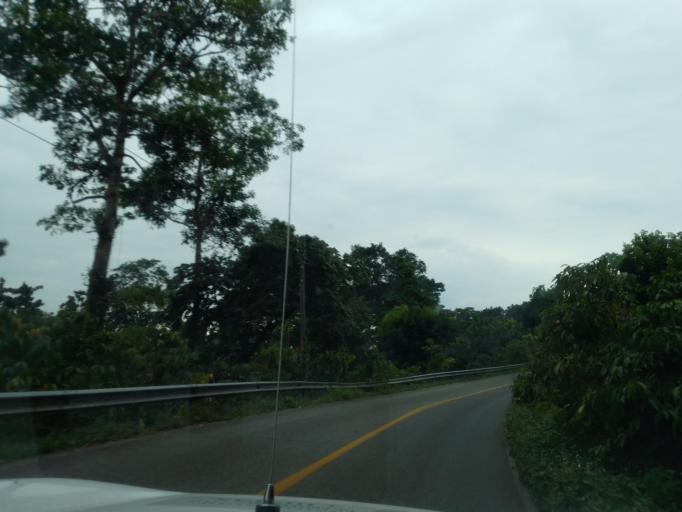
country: MX
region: Chiapas
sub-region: Union Juarez
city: Santo Domingo
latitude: 15.0370
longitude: -92.1227
